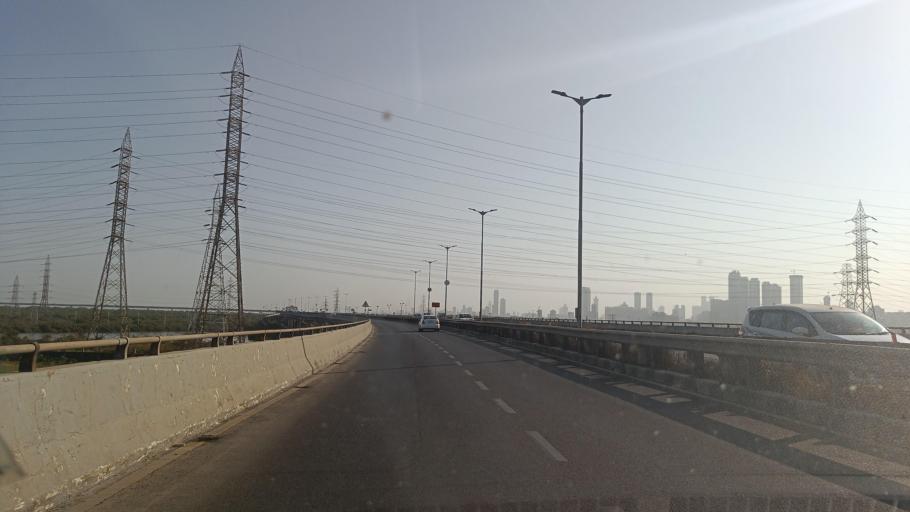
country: IN
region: Maharashtra
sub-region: Mumbai Suburban
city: Mumbai
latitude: 19.0173
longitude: 72.8729
